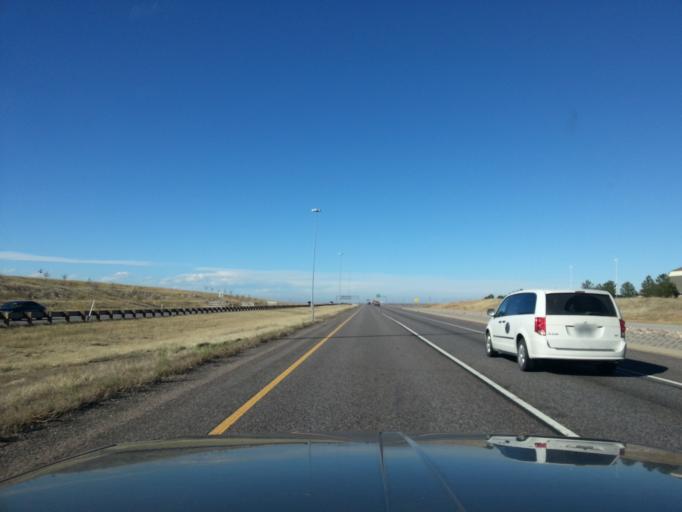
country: US
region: Colorado
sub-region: Adams County
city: Brighton
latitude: 39.8615
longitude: -104.7500
